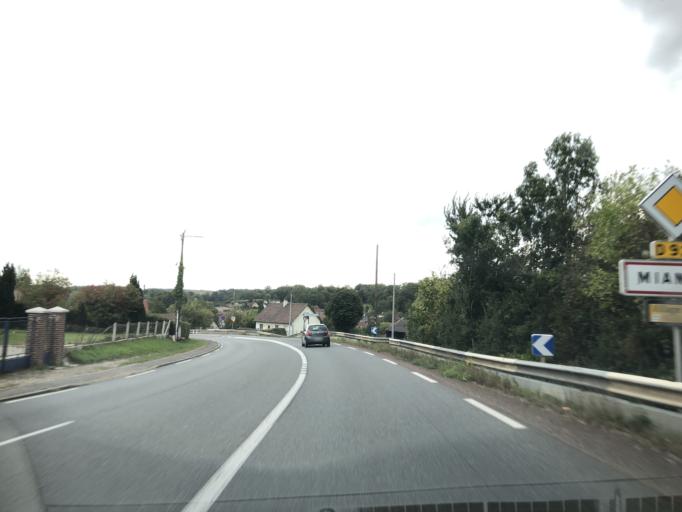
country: FR
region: Picardie
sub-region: Departement de la Somme
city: Chepy
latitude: 50.1002
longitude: 1.7231
